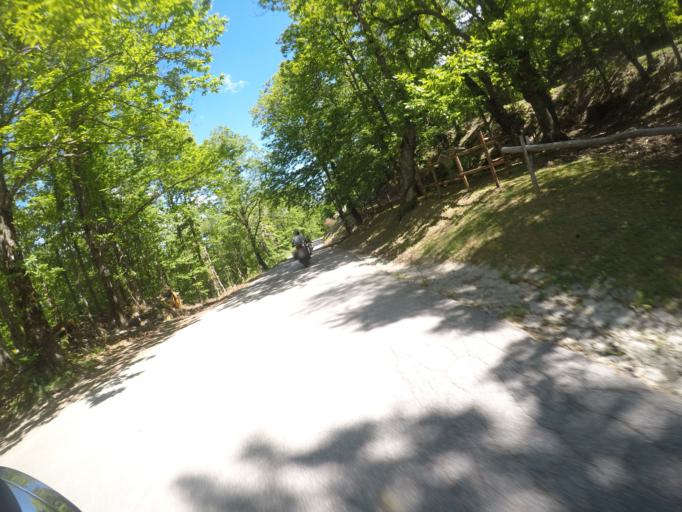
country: IT
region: Tuscany
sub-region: Provincia di Lucca
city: Careggine
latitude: 44.1120
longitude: 10.3288
